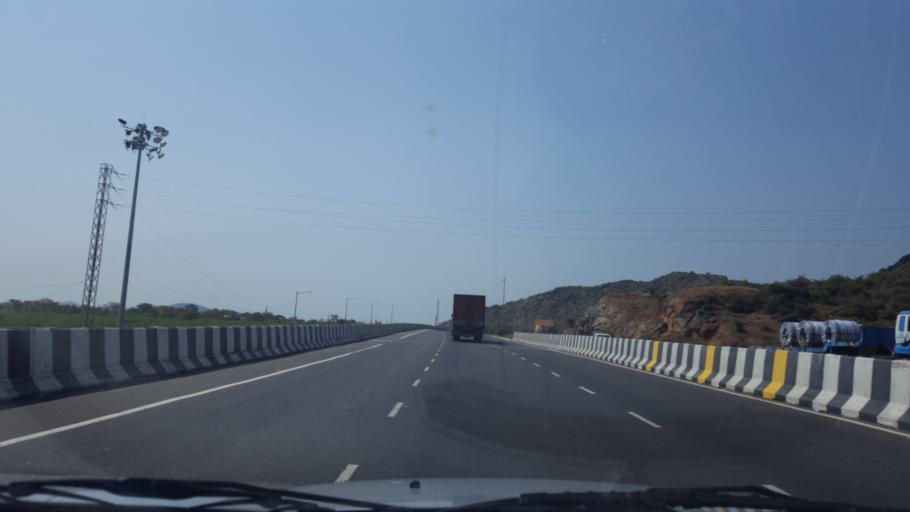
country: IN
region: Andhra Pradesh
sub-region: Prakasam
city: Addanki
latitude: 15.7354
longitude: 80.0152
